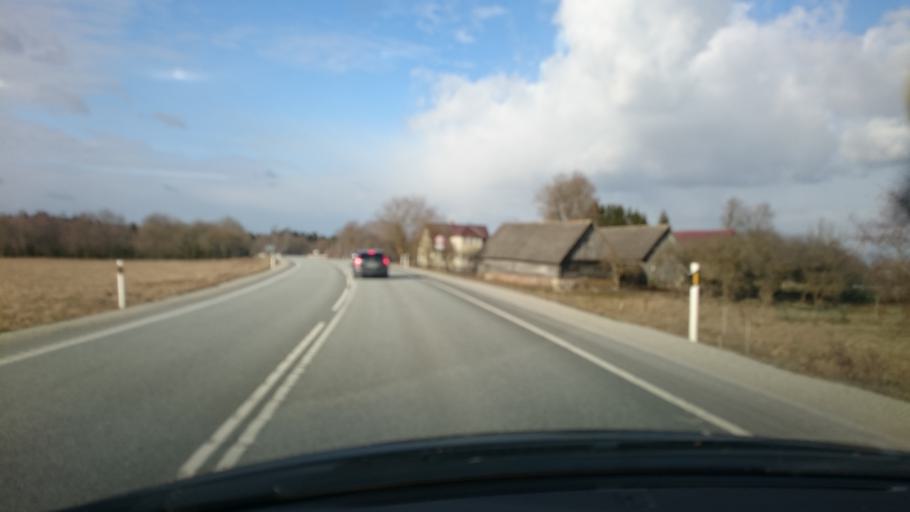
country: EE
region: Harju
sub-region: Keila linn
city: Keila
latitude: 59.2017
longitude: 24.4226
